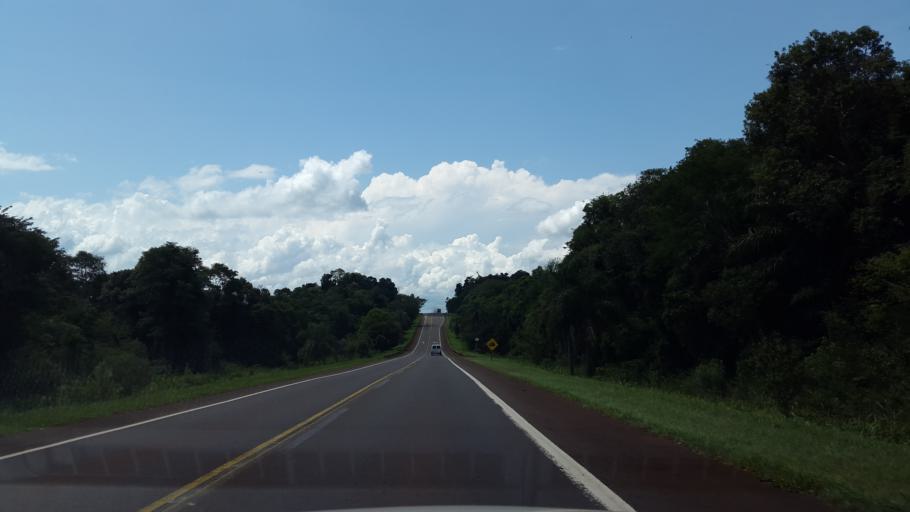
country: AR
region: Misiones
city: El Alcazar
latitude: -26.7019
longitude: -54.8396
